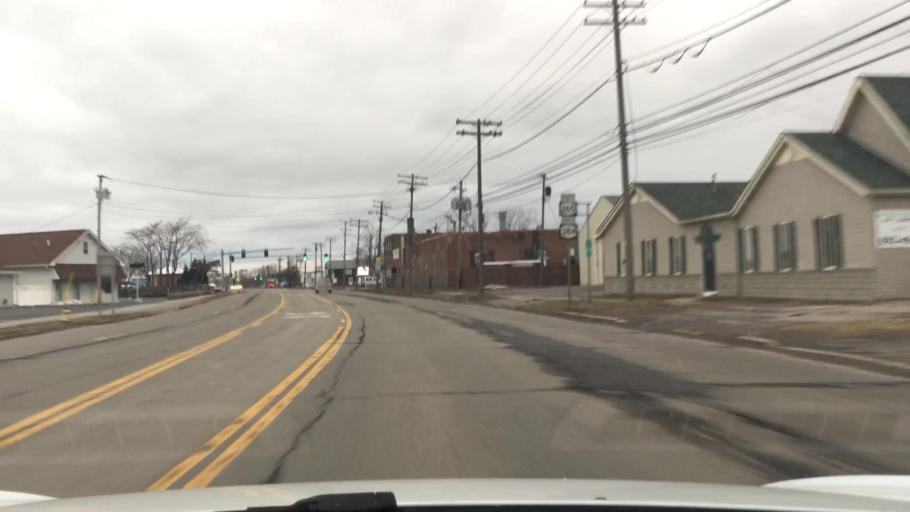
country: US
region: New York
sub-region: Erie County
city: Tonawanda
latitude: 43.0301
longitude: -78.8804
